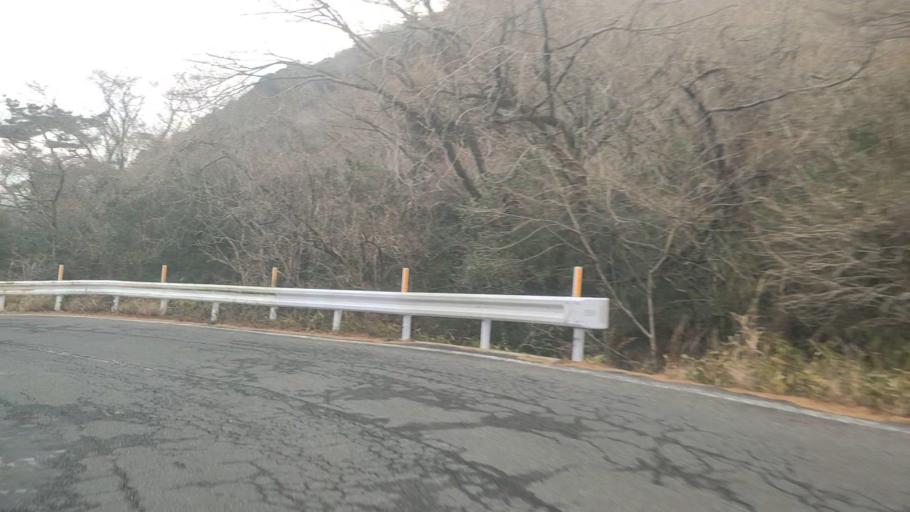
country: JP
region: Nagasaki
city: Shimabara
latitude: 32.7502
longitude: 130.2742
